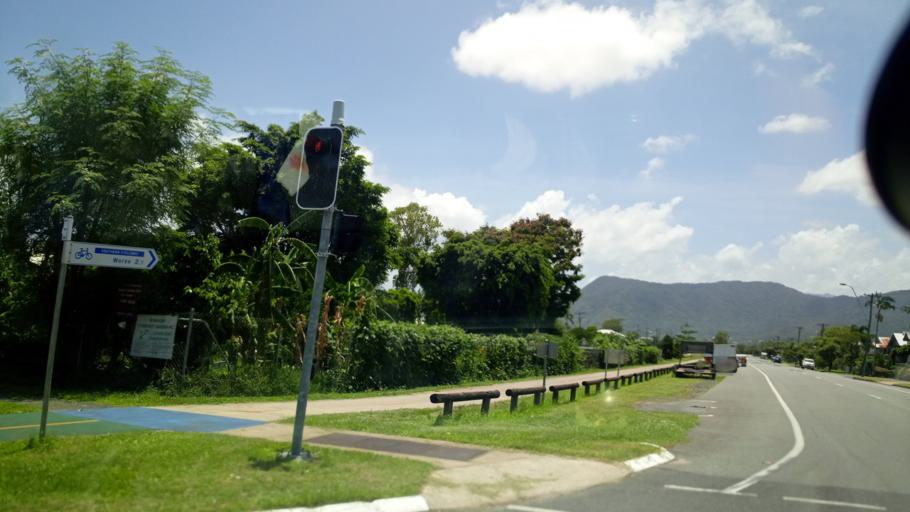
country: AU
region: Queensland
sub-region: Cairns
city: Cairns
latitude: -16.9352
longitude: 145.7625
